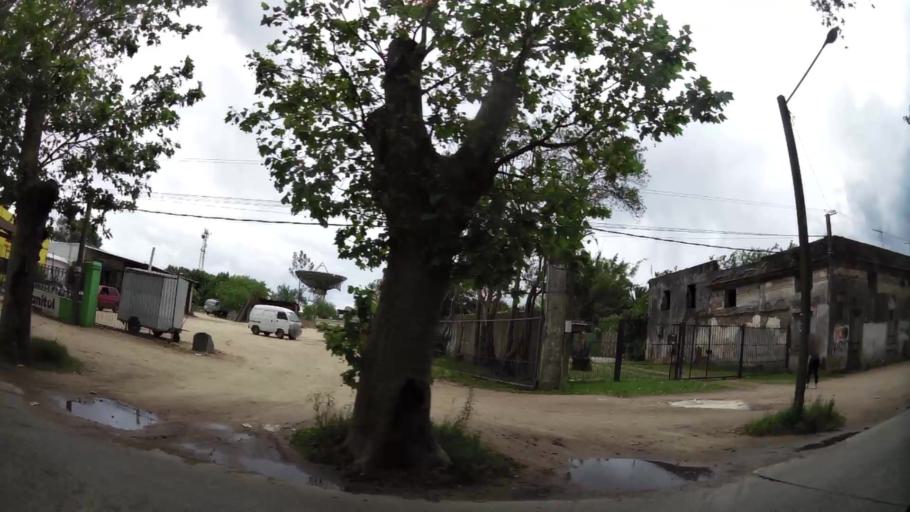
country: UY
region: Canelones
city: Toledo
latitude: -34.8035
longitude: -56.1367
